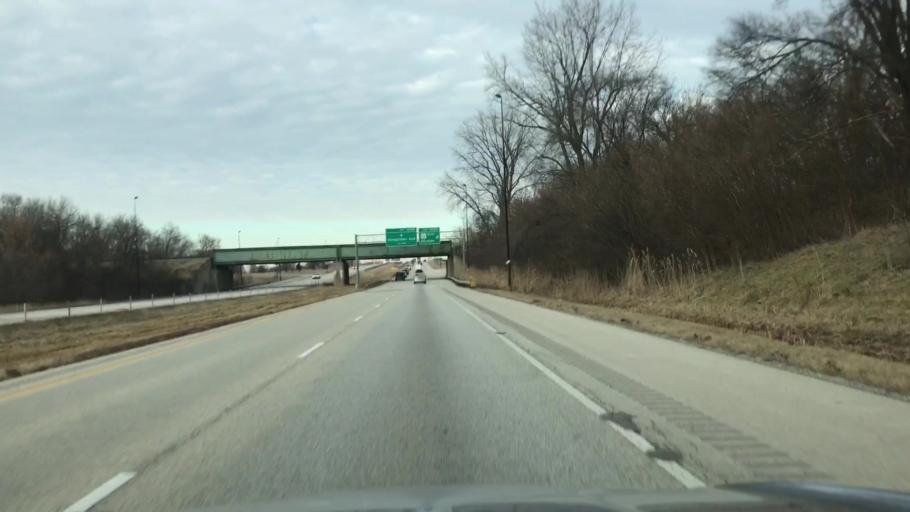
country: US
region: Illinois
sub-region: Sangamon County
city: Grandview
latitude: 39.8260
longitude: -89.5925
